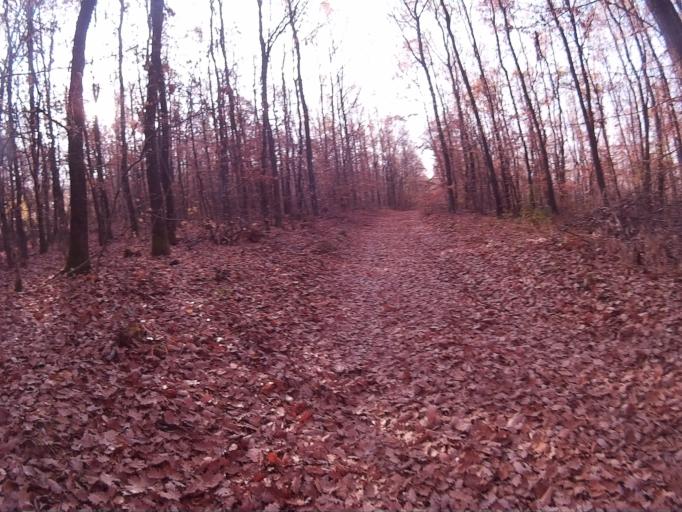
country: HU
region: Heves
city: Belapatfalva
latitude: 48.0086
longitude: 20.3864
